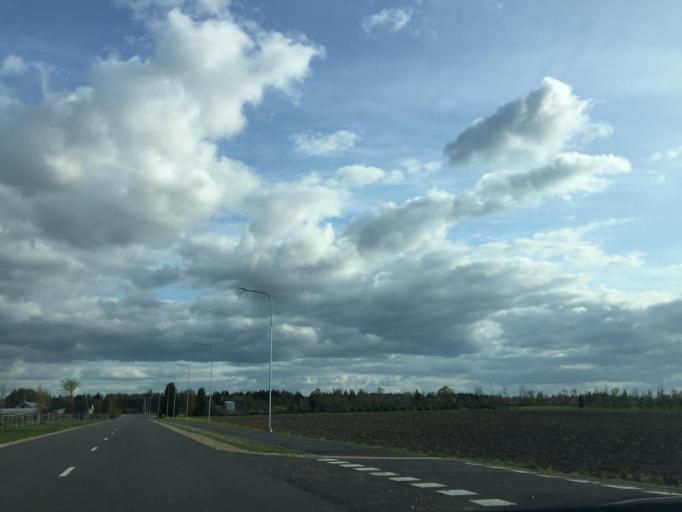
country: LV
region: Sigulda
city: Sigulda
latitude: 57.1356
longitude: 24.8618
